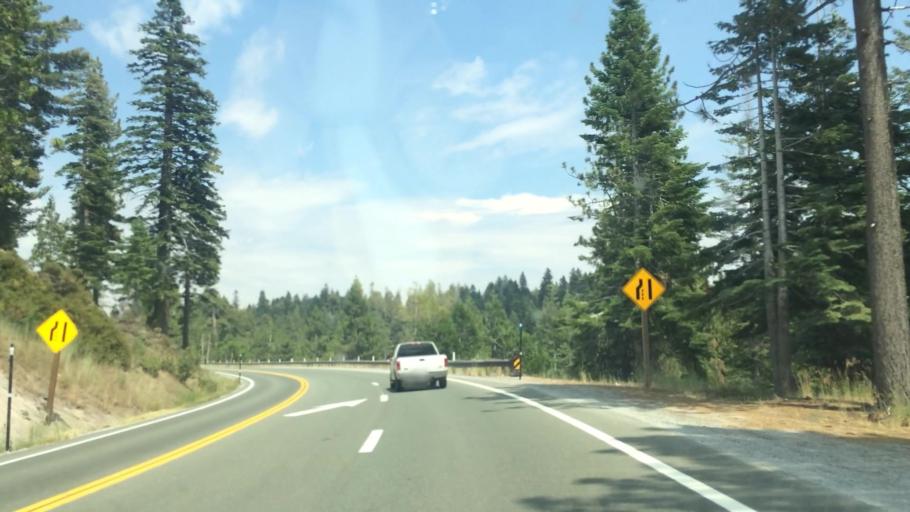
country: US
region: California
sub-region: Amador County
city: Pioneer
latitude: 38.5453
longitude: -120.3128
